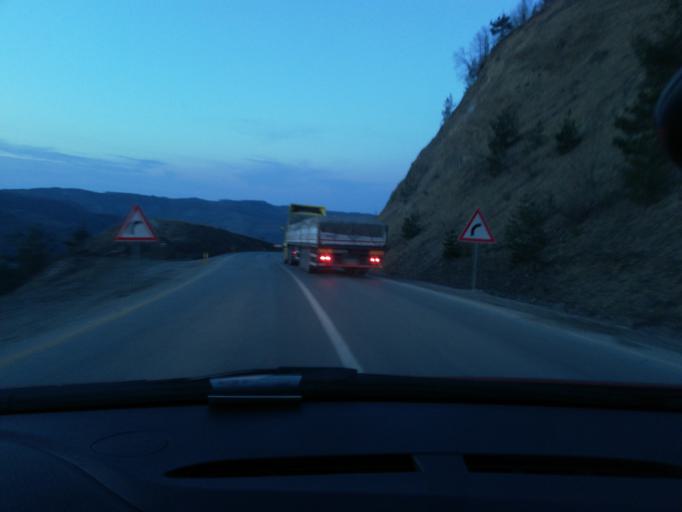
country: TR
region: Kastamonu
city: Inebolu
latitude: 41.9144
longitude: 33.7265
